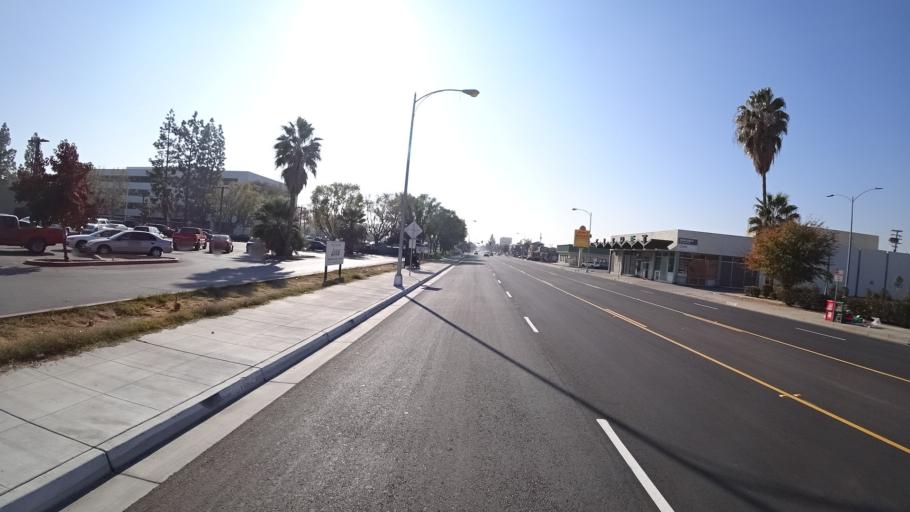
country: US
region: California
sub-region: Kern County
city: Bakersfield
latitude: 35.3885
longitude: -119.0234
